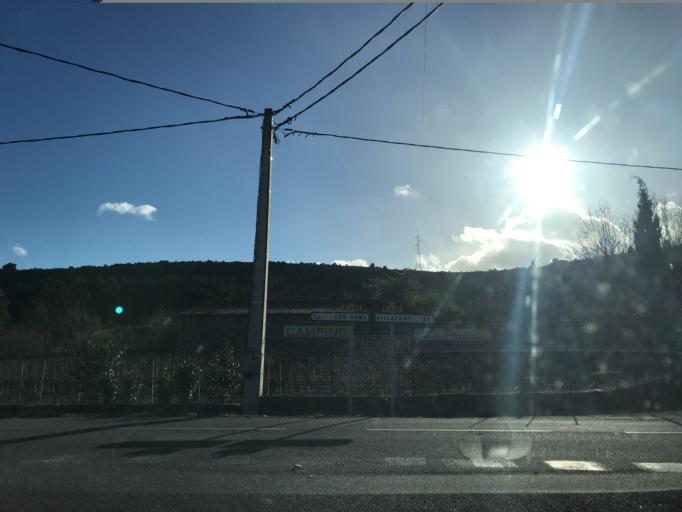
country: FR
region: Rhone-Alpes
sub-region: Departement de l'Ardeche
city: Les Vans
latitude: 44.4088
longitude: 4.1106
